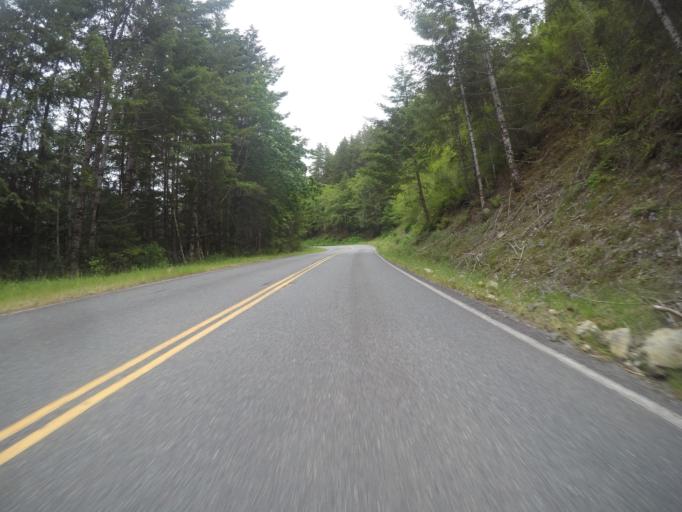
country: US
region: California
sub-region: Del Norte County
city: Bertsch-Oceanview
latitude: 41.7666
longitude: -124.0088
